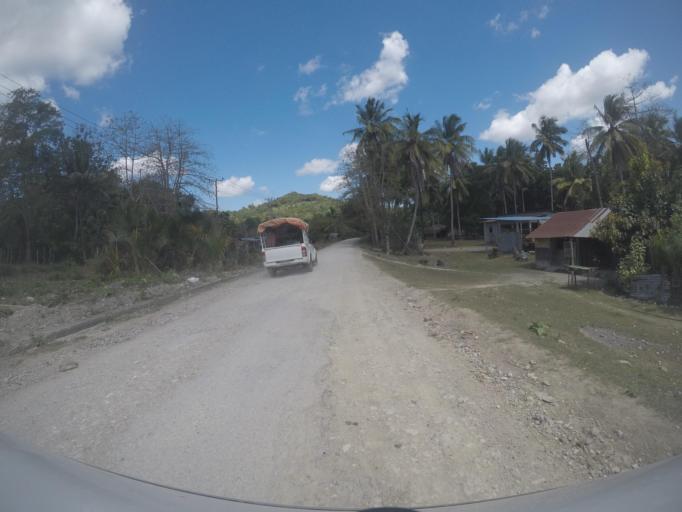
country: TL
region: Viqueque
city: Viqueque
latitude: -8.8973
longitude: 126.3915
